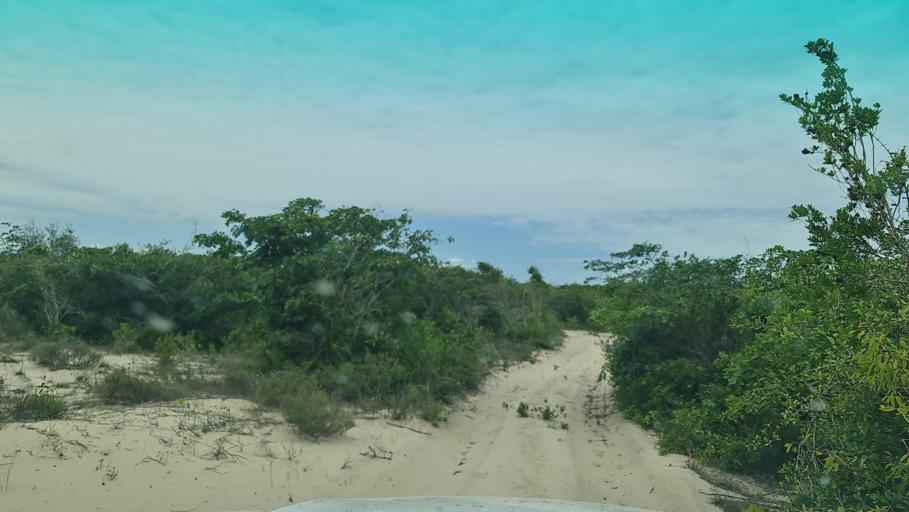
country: MZ
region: Maputo
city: Manhica
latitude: -25.6403
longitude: 32.7819
